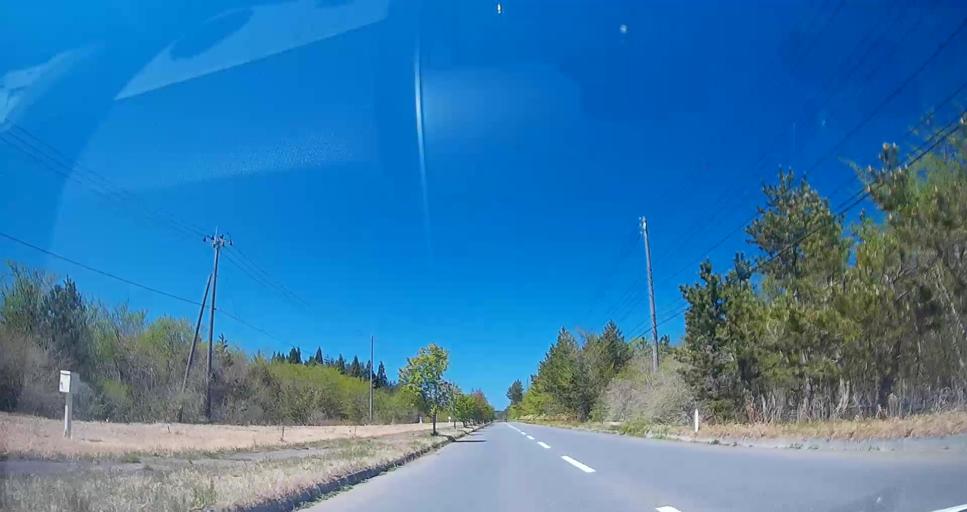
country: JP
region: Aomori
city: Misawa
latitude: 40.9439
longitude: 141.3710
